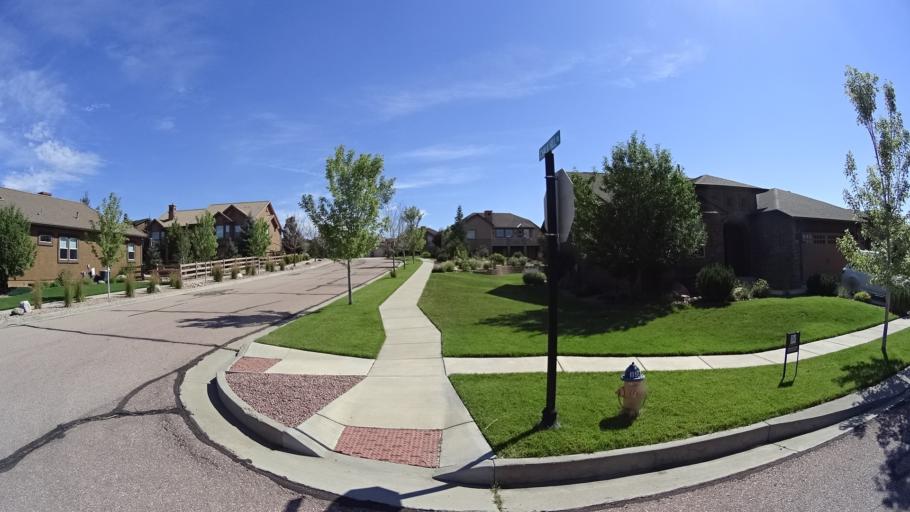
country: US
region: Colorado
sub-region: El Paso County
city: Gleneagle
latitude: 39.0257
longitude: -104.8025
